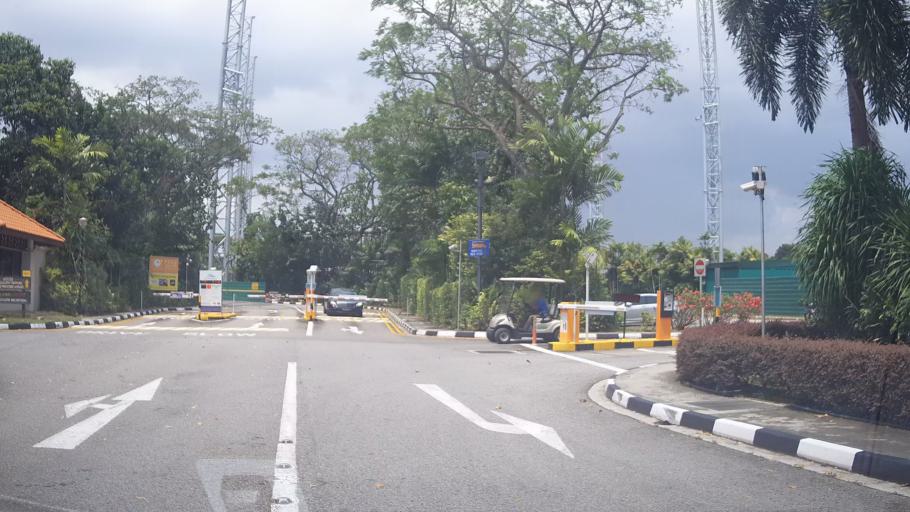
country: SG
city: Singapore
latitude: 1.3170
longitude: 103.9755
